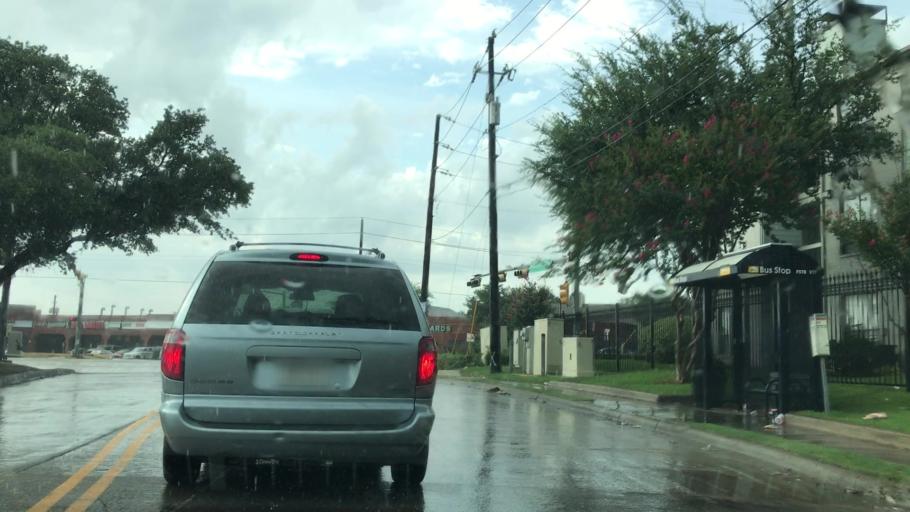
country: US
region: Texas
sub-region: Dallas County
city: Richardson
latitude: 32.9033
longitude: -96.7133
